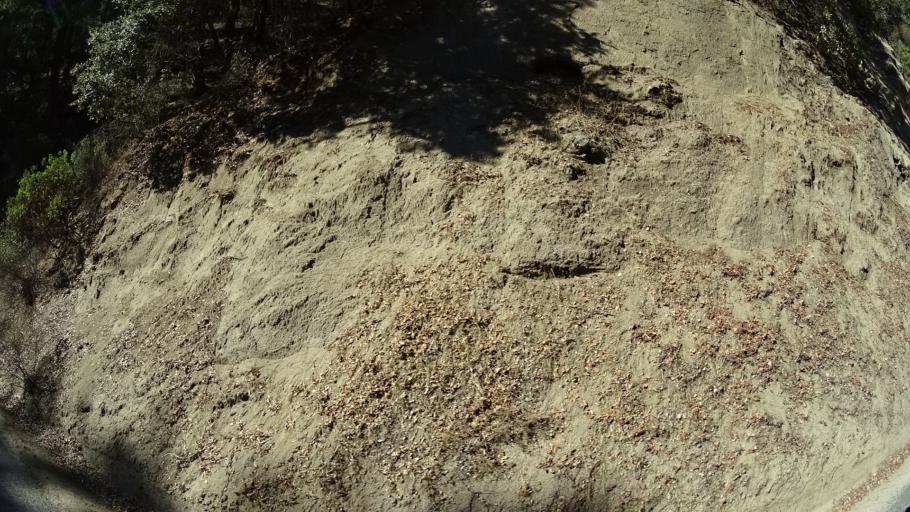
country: US
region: California
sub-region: Siskiyou County
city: Happy Camp
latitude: 41.2940
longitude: -123.2435
